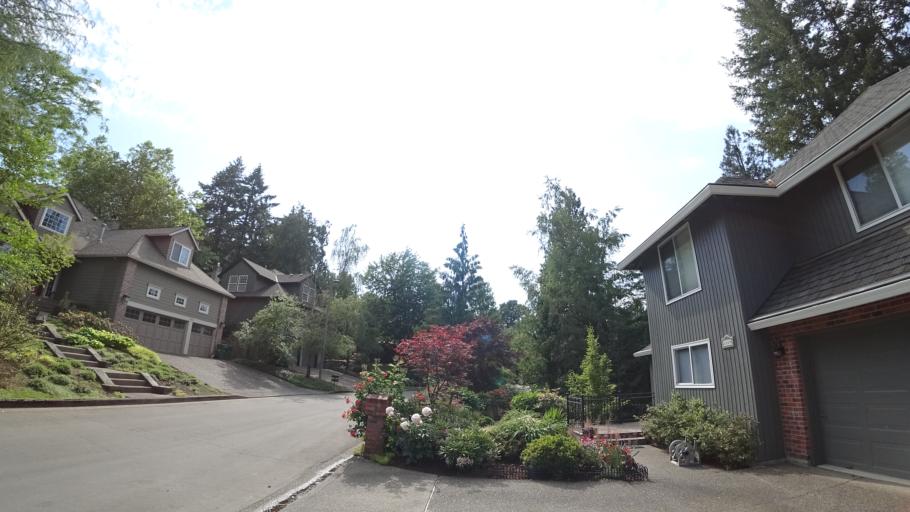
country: US
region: Oregon
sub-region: Washington County
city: Garden Home-Whitford
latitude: 45.4588
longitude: -122.7442
